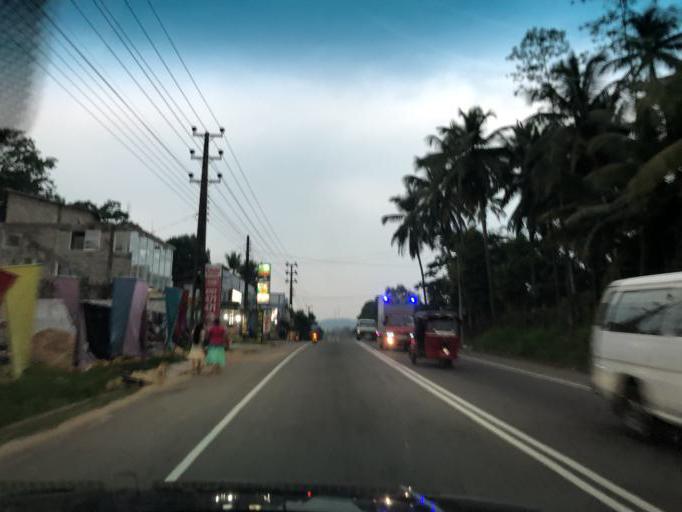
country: LK
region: Western
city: Horana South
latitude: 6.7231
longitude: 80.0805
